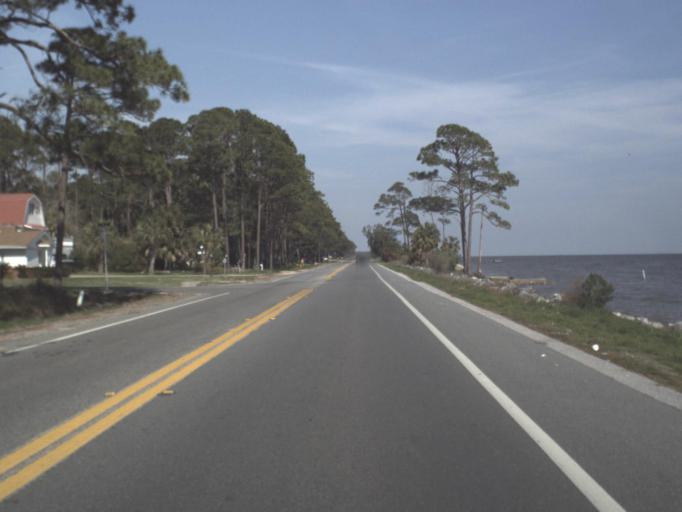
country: US
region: Florida
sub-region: Franklin County
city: Eastpoint
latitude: 29.7448
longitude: -84.8637
